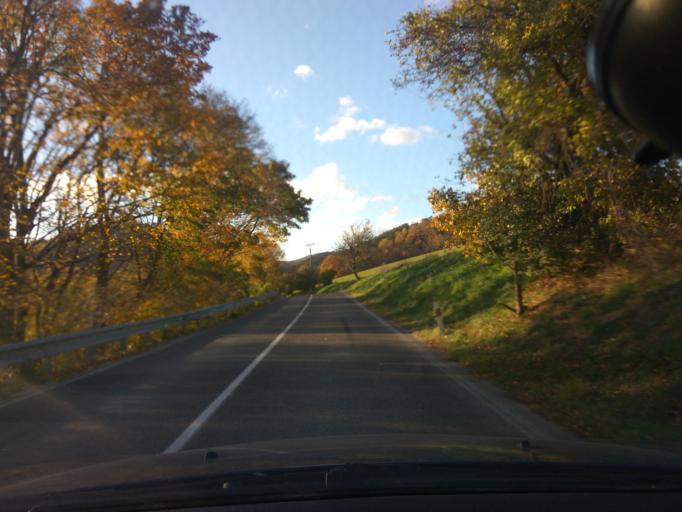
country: SK
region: Trnavsky
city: Vrbove
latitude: 48.6425
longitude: 17.6448
